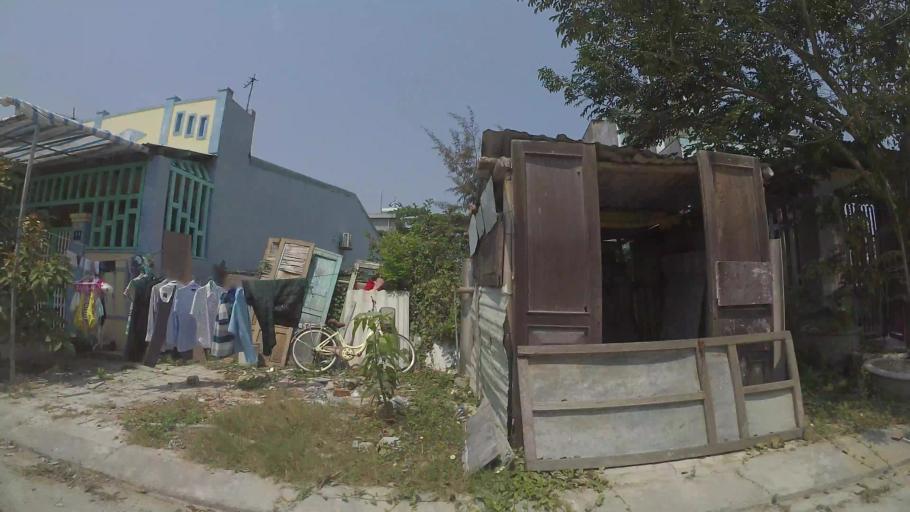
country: VN
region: Da Nang
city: Ngu Hanh Son
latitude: 15.9764
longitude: 108.2594
